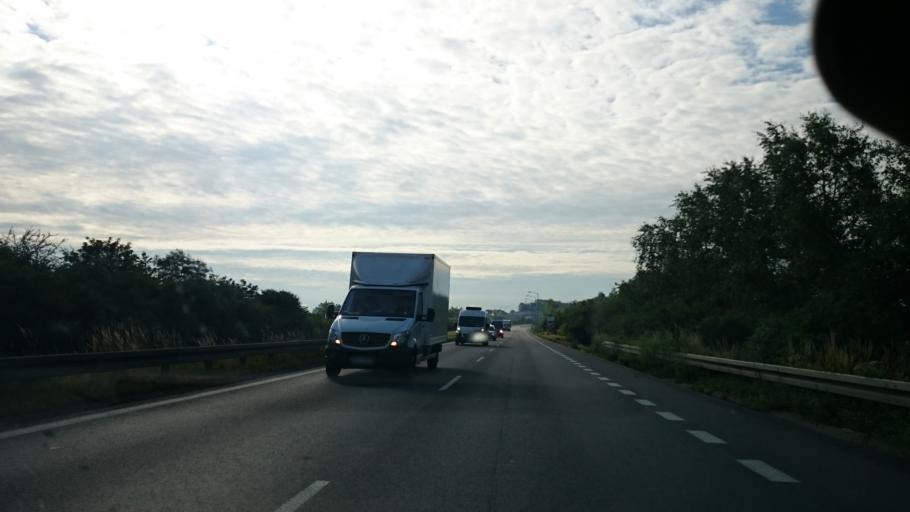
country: PL
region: Opole Voivodeship
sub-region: Powiat opolski
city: Opole
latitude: 50.7001
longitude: 17.9498
